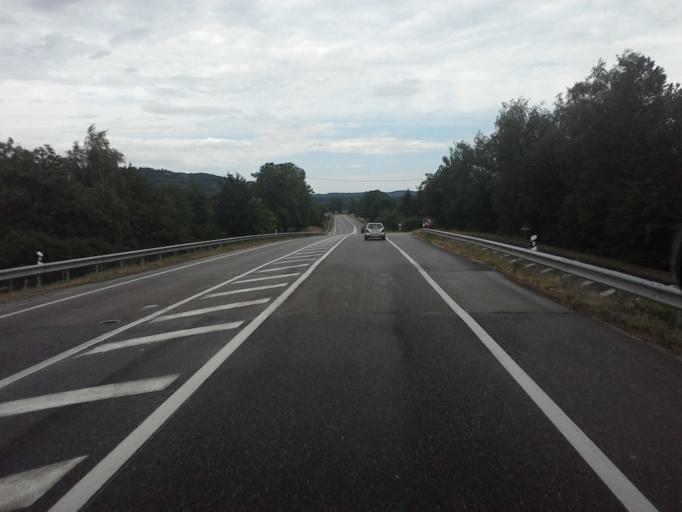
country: FR
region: Franche-Comte
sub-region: Departement du Jura
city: Poligny
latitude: 46.8445
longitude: 5.7021
